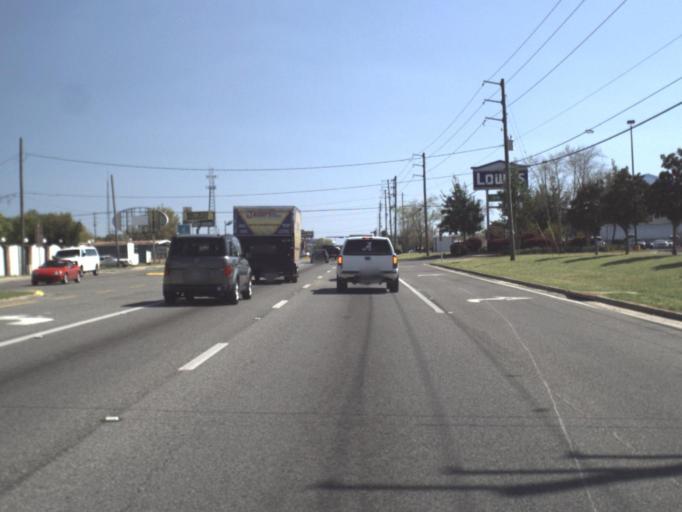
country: US
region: Florida
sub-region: Okaloosa County
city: Wright
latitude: 30.4445
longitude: -86.6387
